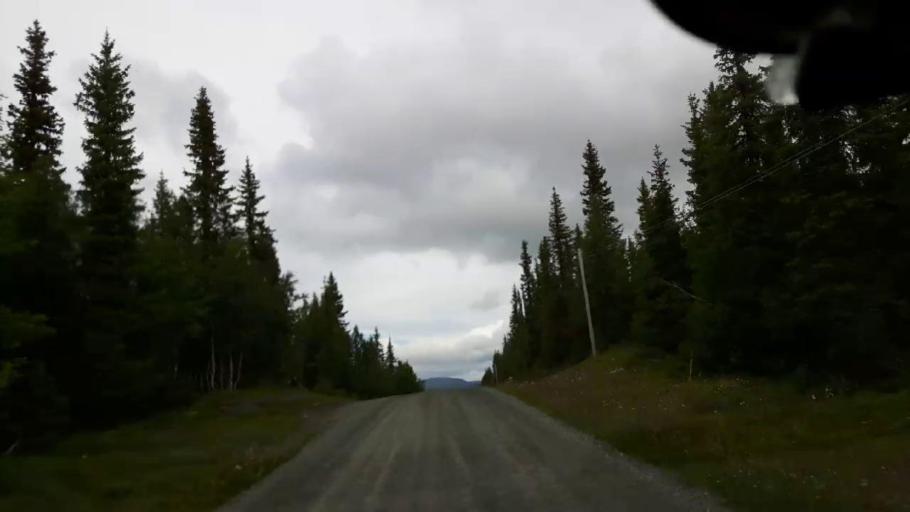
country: SE
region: Jaemtland
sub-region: Krokoms Kommun
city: Valla
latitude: 63.7722
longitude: 13.8295
